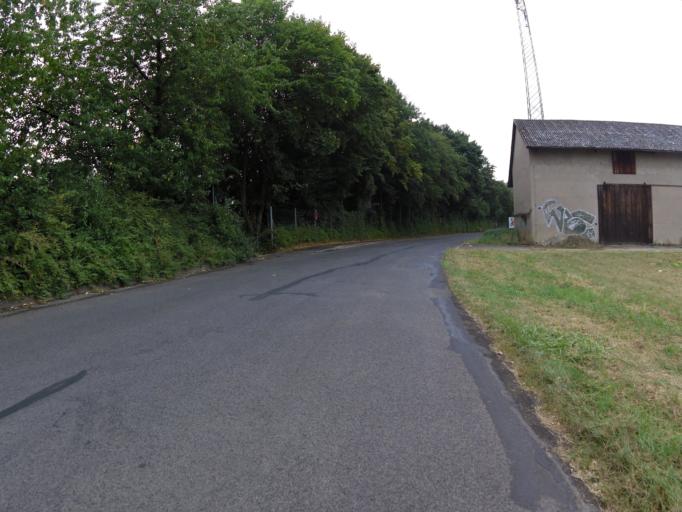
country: DE
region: Bavaria
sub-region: Regierungsbezirk Unterfranken
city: Guntersleben
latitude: 49.8759
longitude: 9.9109
